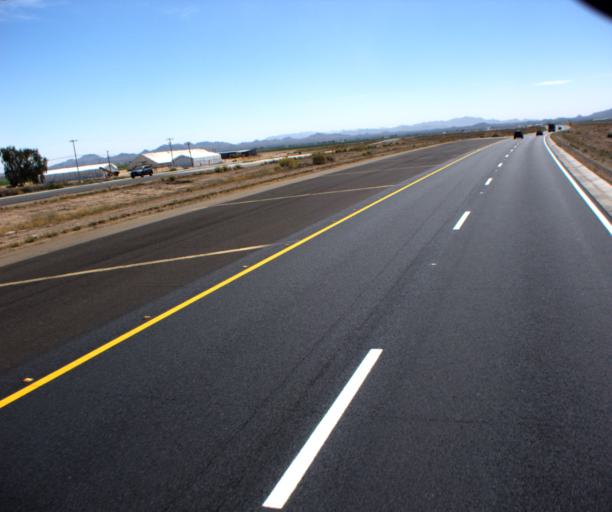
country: US
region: Arizona
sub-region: Maricopa County
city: Buckeye
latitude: 33.4115
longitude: -112.6266
